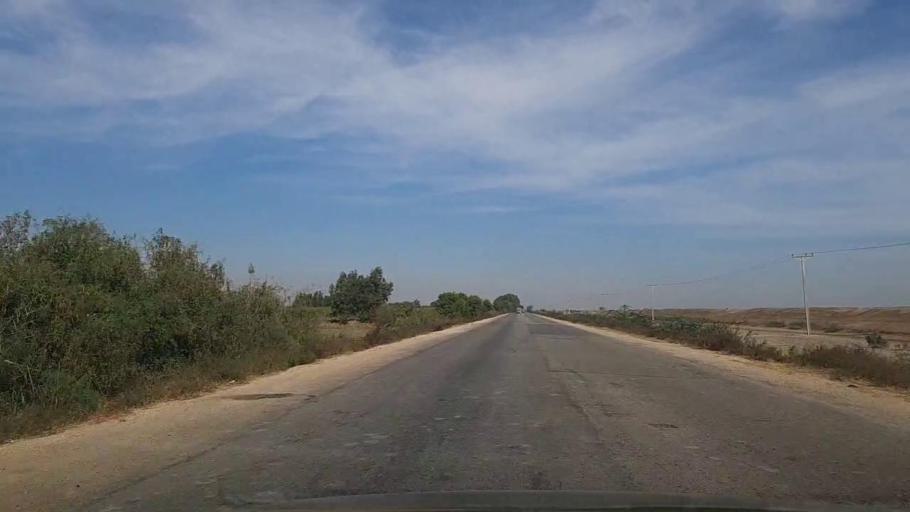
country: PK
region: Sindh
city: Daro Mehar
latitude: 24.9525
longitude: 68.1140
